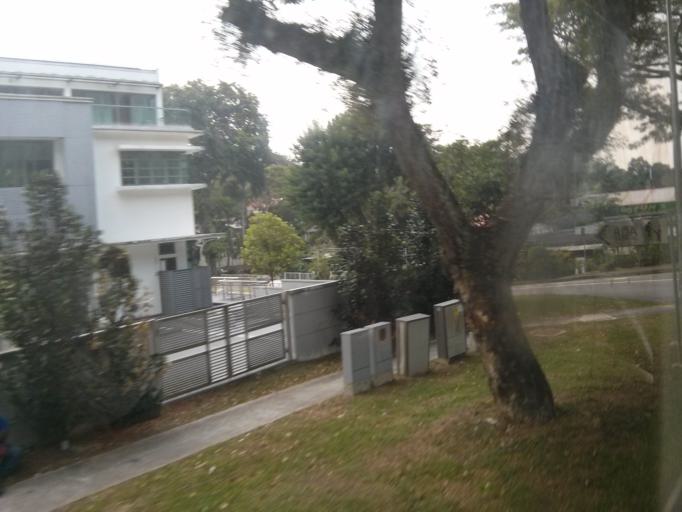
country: SG
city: Singapore
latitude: 1.3351
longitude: 103.8369
